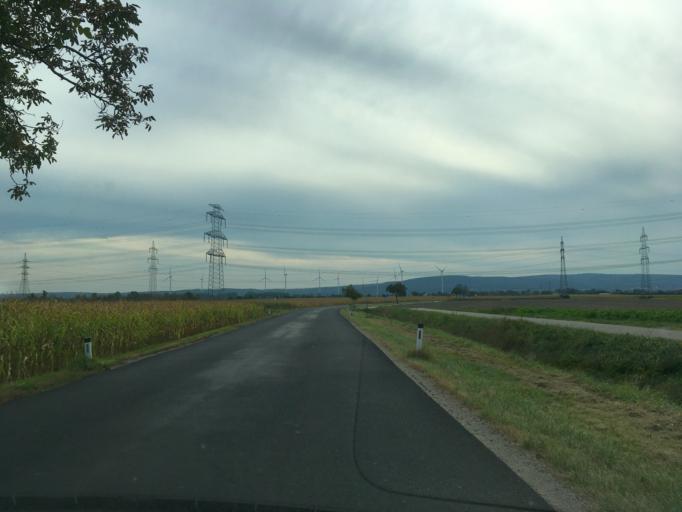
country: AT
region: Lower Austria
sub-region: Politischer Bezirk Bruck an der Leitha
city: Trautmannsdorf an der Leitha
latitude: 48.0334
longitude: 16.6779
